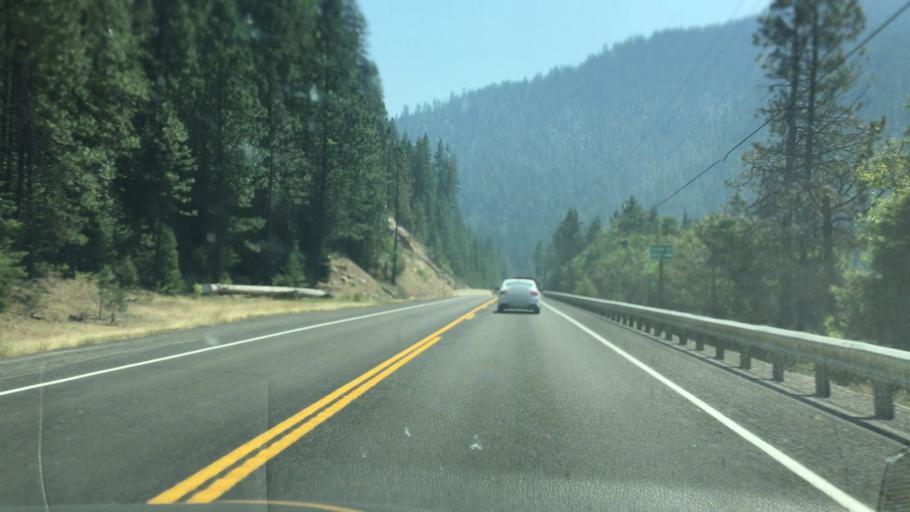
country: US
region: Idaho
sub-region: Valley County
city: McCall
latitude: 45.1557
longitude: -116.2980
